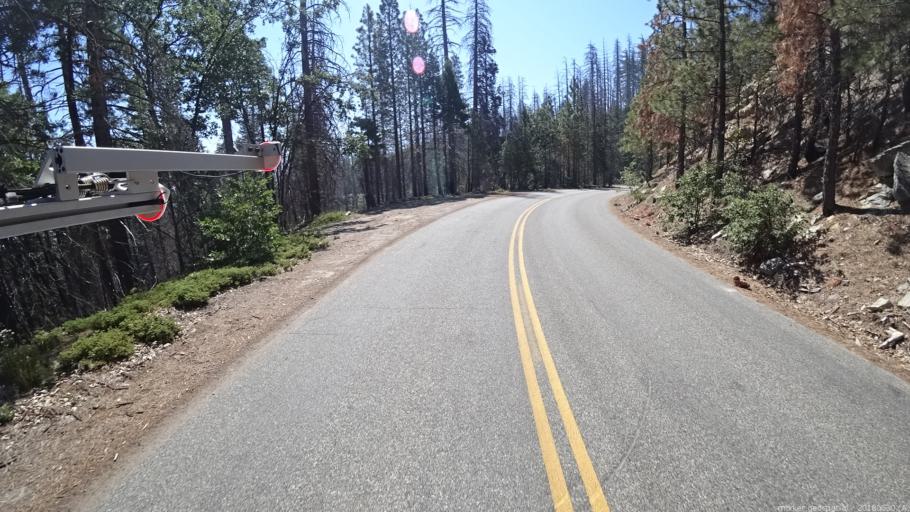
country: US
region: California
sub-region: Fresno County
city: Auberry
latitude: 37.3219
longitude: -119.3656
